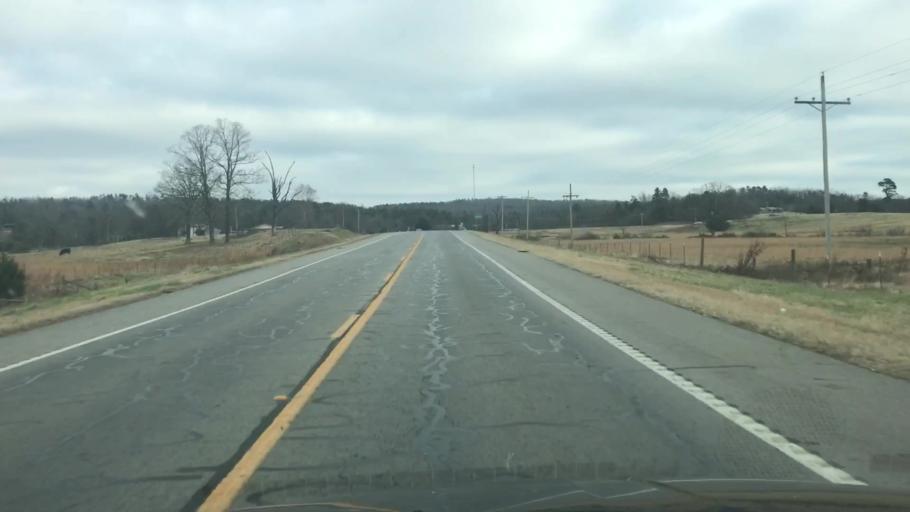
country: US
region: Arkansas
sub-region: Scott County
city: Waldron
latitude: 34.8047
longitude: -94.0405
